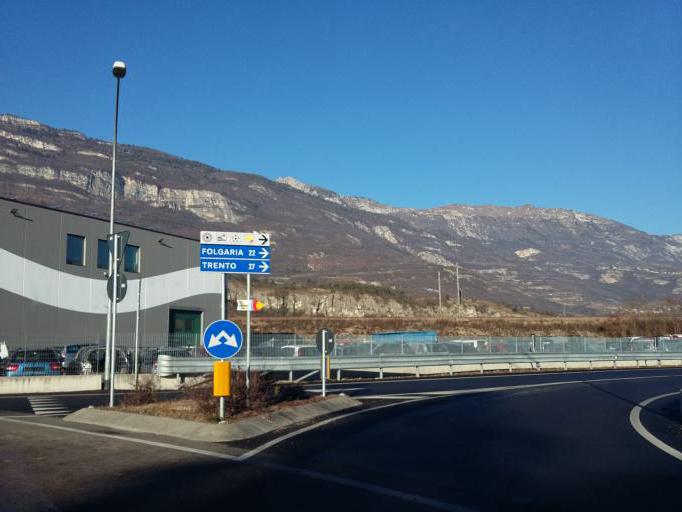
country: IT
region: Trentino-Alto Adige
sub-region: Provincia di Trento
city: Rovereto
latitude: 45.8726
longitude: 11.0209
